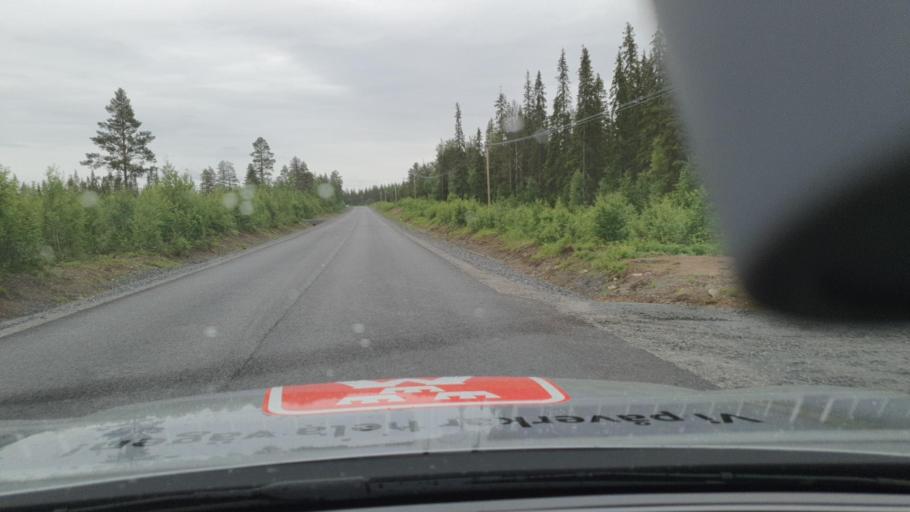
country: SE
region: Norrbotten
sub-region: Overkalix Kommun
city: OEverkalix
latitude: 66.7195
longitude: 23.1889
